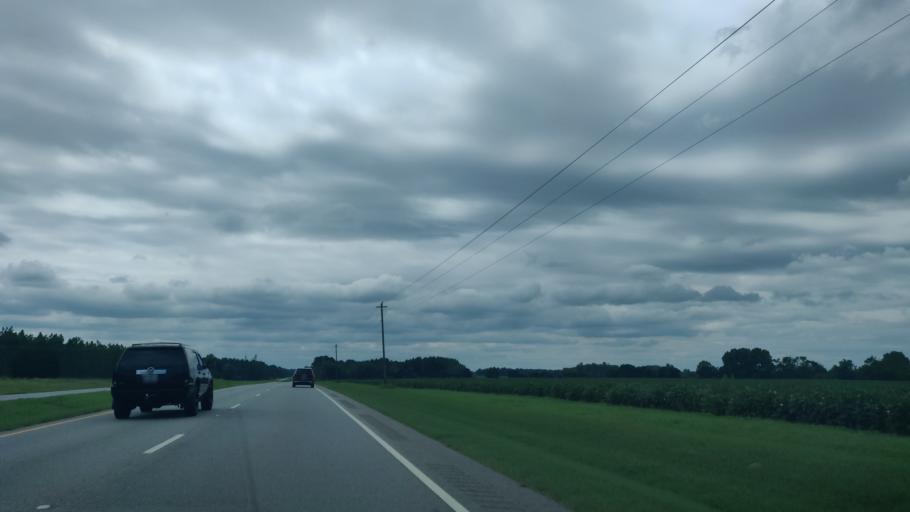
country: US
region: Georgia
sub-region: Terrell County
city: Dawson
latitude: 31.8166
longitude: -84.4573
